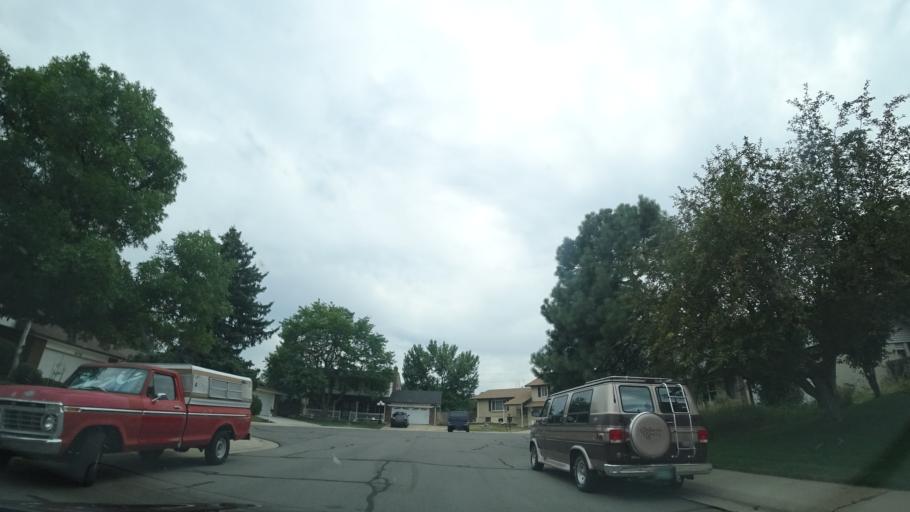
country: US
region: Colorado
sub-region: Jefferson County
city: Lakewood
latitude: 39.7046
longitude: -105.0955
